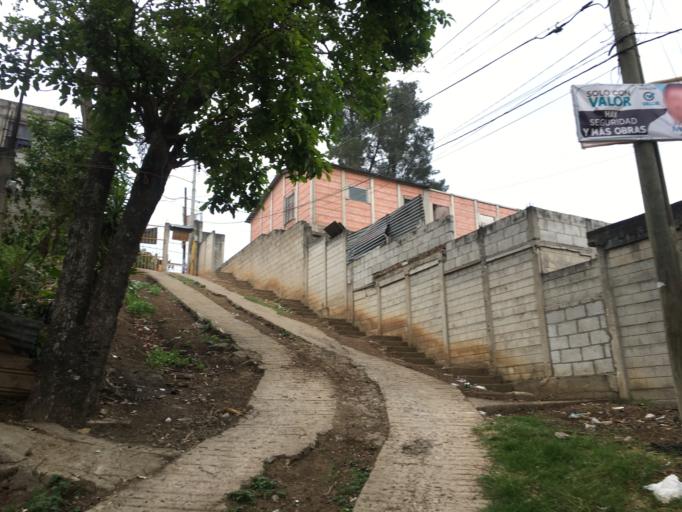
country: GT
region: Guatemala
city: Petapa
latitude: 14.5062
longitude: -90.5524
